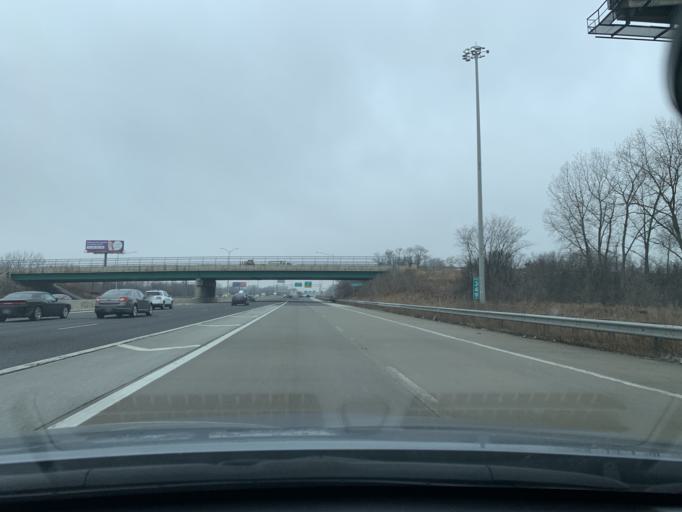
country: US
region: Illinois
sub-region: Cook County
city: Markham
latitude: 41.6125
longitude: -87.6953
